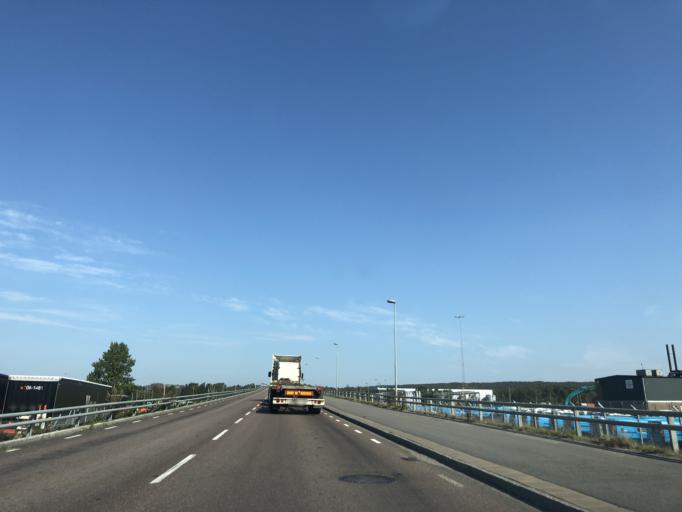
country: SE
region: Vaestra Goetaland
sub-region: Goteborg
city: Majorna
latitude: 57.6964
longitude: 11.8601
